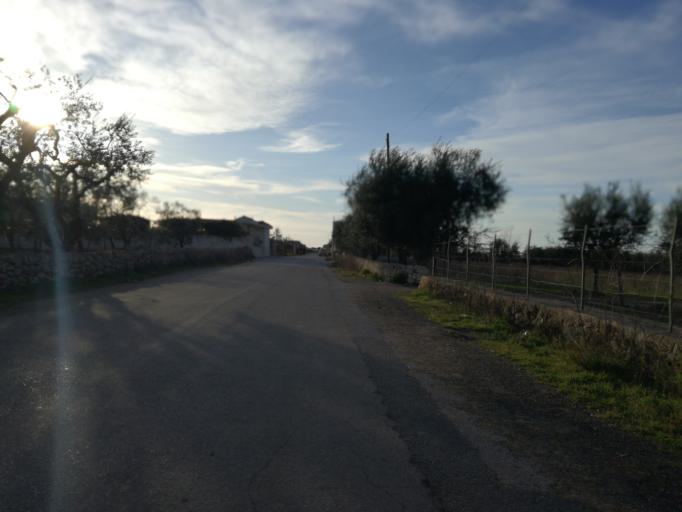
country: IT
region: Apulia
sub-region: Provincia di Bari
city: Capurso
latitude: 41.0499
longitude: 16.9061
